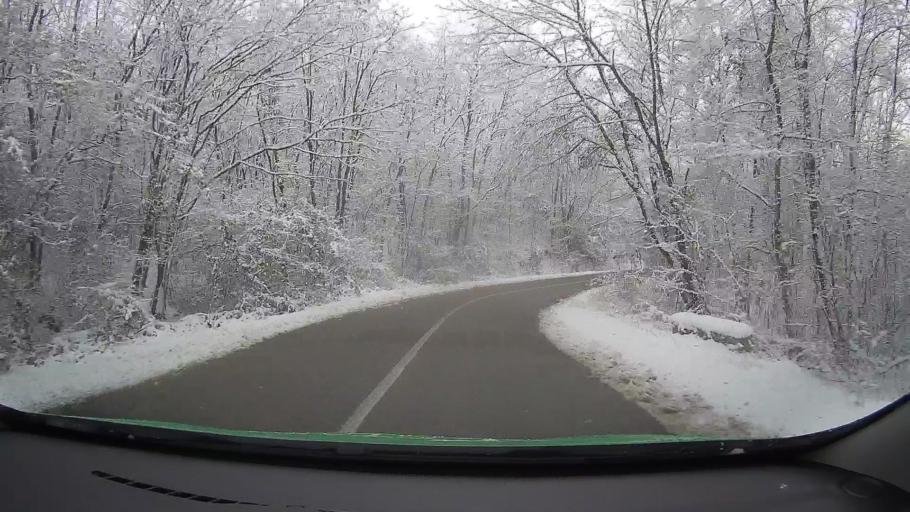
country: RO
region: Hunedoara
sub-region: Oras Hateg
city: Hateg
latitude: 45.6380
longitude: 22.9182
